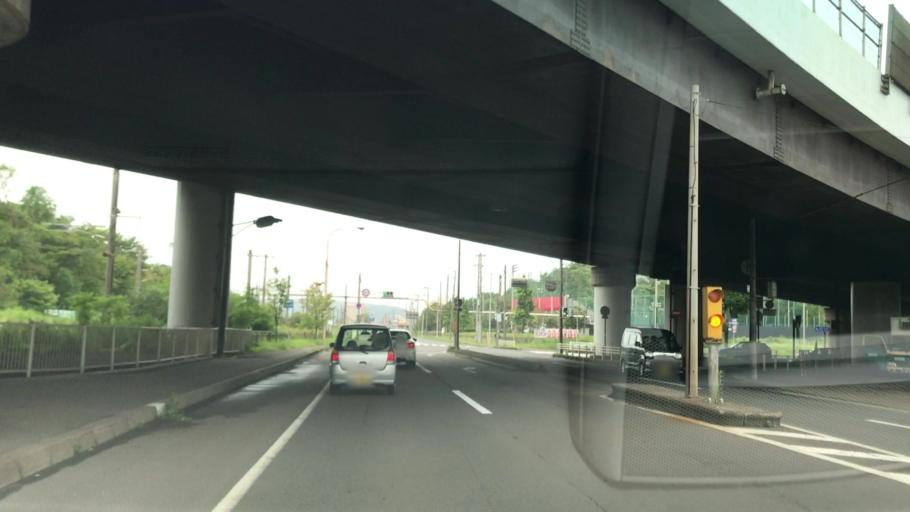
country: JP
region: Hokkaido
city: Muroran
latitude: 42.3378
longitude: 141.0142
